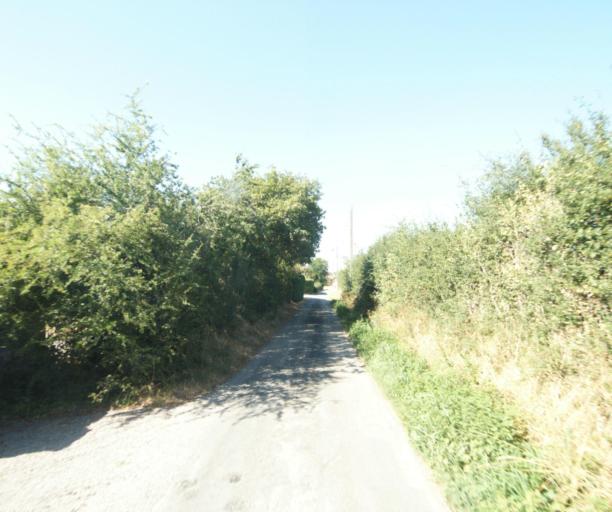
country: FR
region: Rhone-Alpes
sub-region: Departement du Rhone
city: La Tour-de-Salvagny
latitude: 45.8304
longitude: 4.7259
